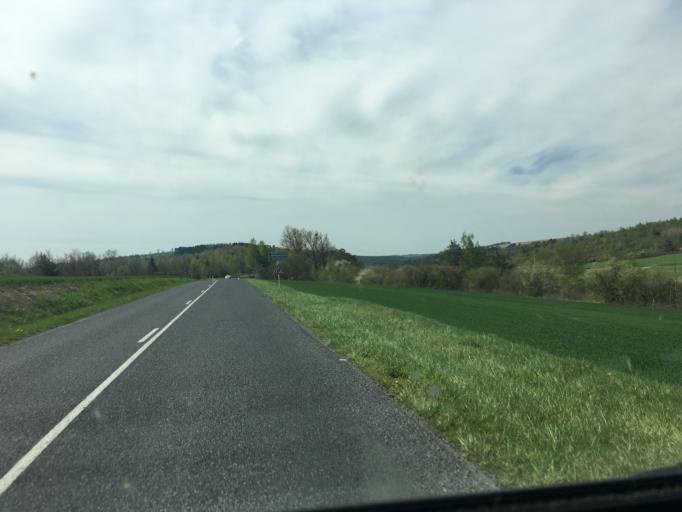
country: FR
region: Lorraine
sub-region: Departement de la Meuse
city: Saint-Mihiel
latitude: 48.8504
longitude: 5.5154
